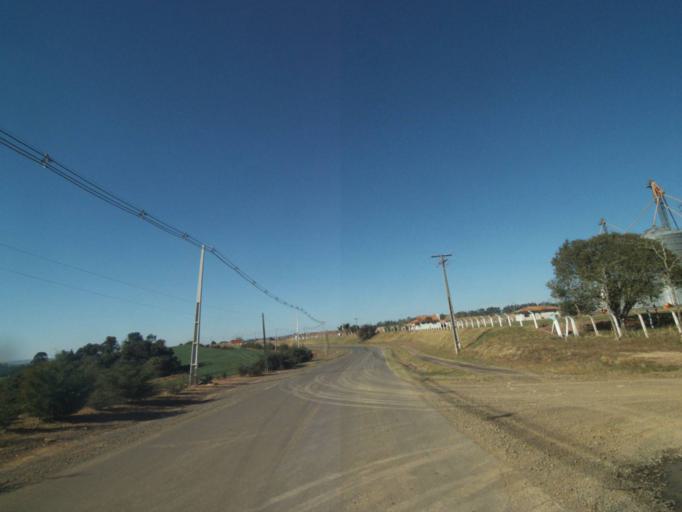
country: BR
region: Parana
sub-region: Tibagi
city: Tibagi
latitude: -24.5260
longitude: -50.4383
